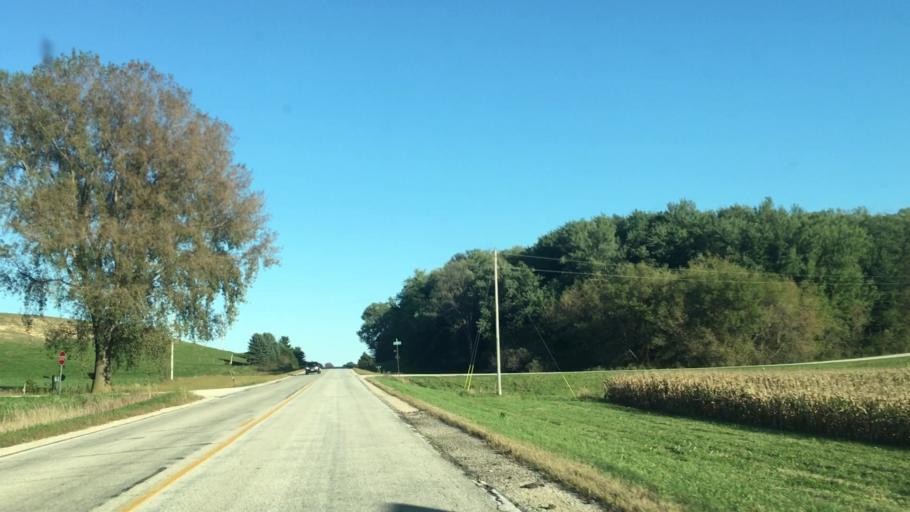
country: US
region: Minnesota
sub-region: Fillmore County
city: Chatfield
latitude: 43.8450
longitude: -92.1002
